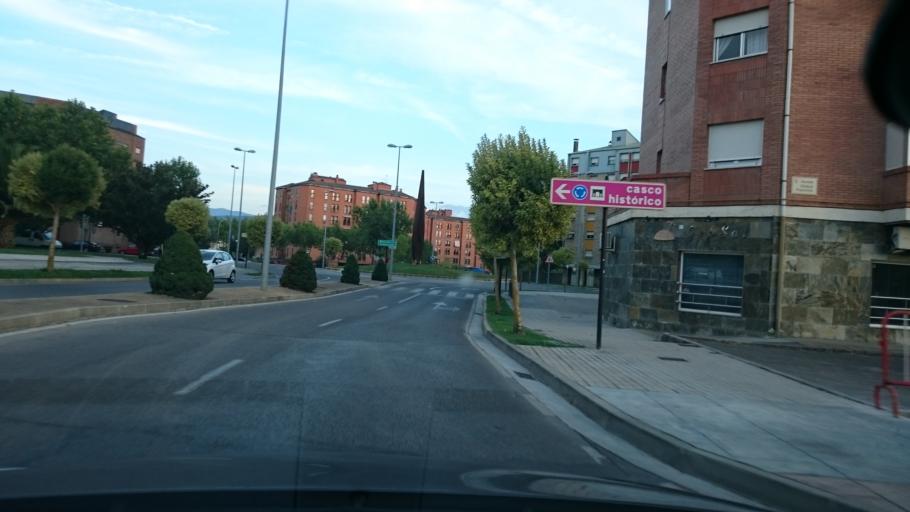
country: ES
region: Castille and Leon
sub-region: Provincia de Leon
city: Ponferrada
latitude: 42.5561
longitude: -6.5957
